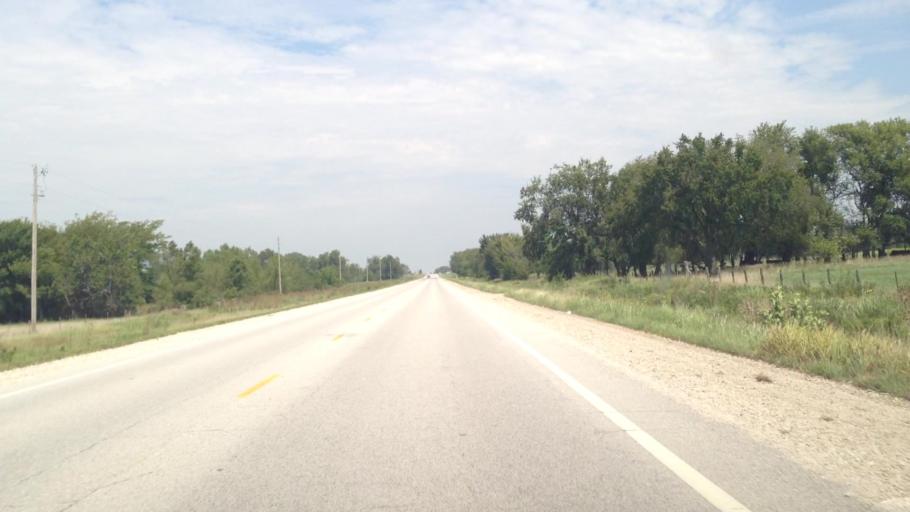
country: US
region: Kansas
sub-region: Neosho County
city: Erie
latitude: 37.4629
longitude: -95.2695
